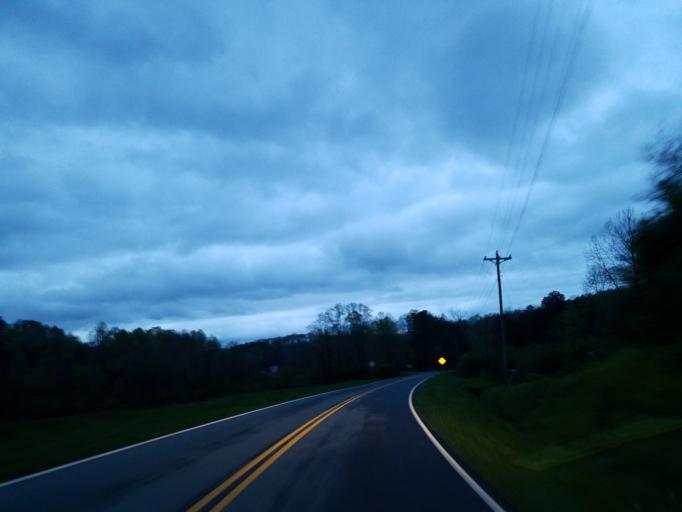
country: US
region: Georgia
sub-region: Gilmer County
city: Ellijay
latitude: 34.6726
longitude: -84.3834
